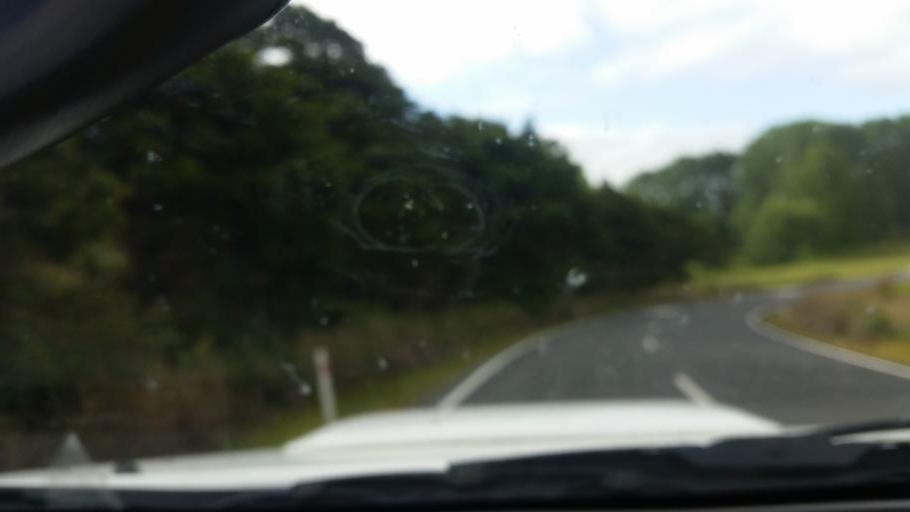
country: NZ
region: Northland
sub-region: Kaipara District
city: Dargaville
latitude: -35.8393
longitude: 173.8446
